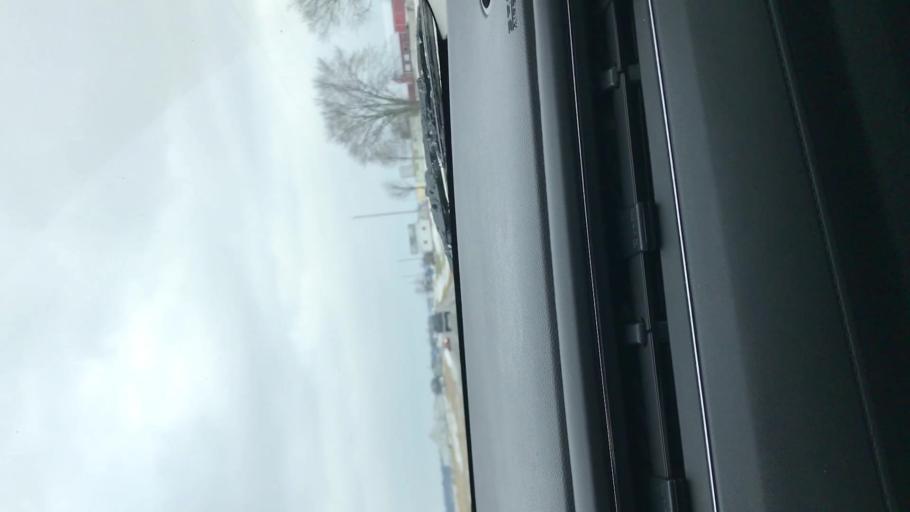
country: US
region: Ohio
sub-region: Hardin County
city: Kenton
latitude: 40.7529
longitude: -83.6335
